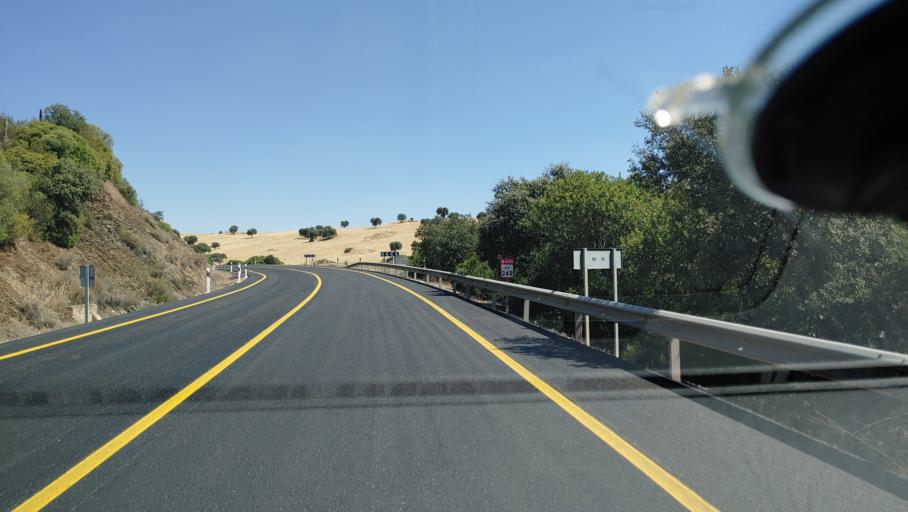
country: ES
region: Castille-La Mancha
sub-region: Provincia de Ciudad Real
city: Saceruela
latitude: 39.0137
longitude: -4.4639
